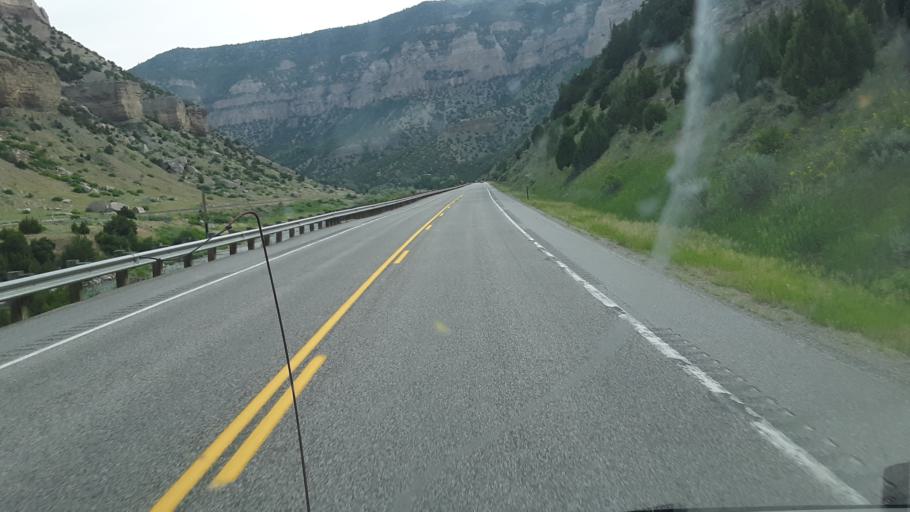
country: US
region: Wyoming
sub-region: Hot Springs County
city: Thermopolis
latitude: 43.4842
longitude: -108.1665
